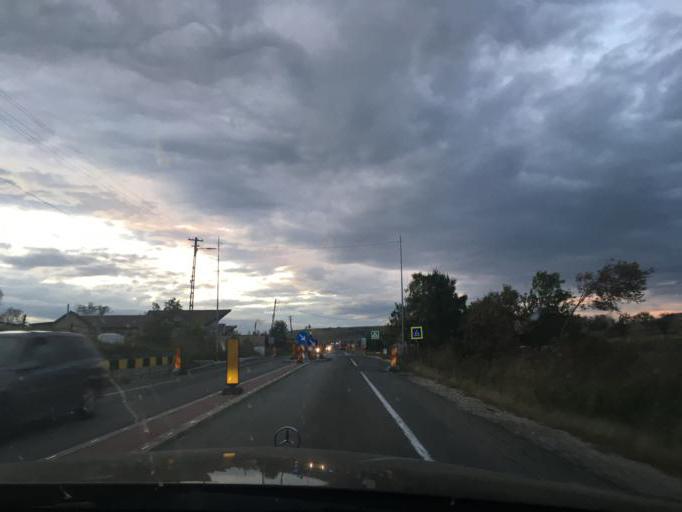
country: RO
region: Cluj
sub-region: Comuna Izvoru Crisului
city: Izvoru Crisului
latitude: 46.8157
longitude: 23.1787
